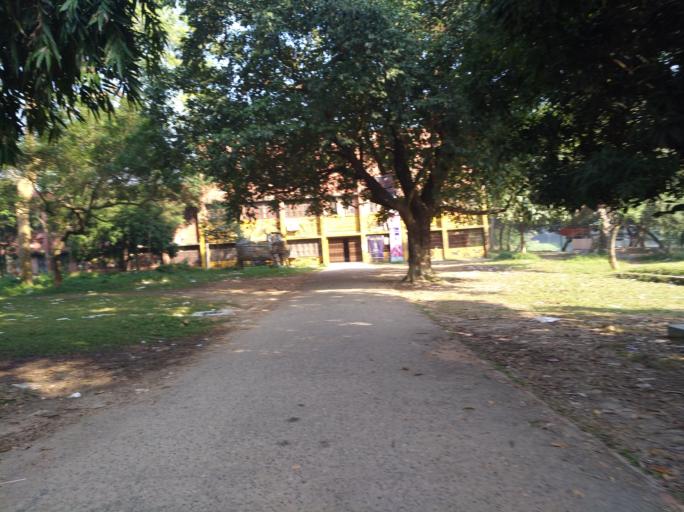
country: BD
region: Dhaka
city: Tungi
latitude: 23.8872
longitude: 90.2660
